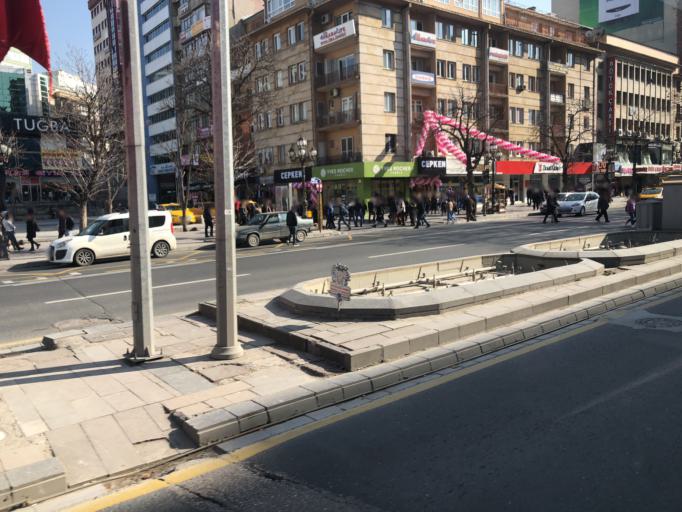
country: TR
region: Ankara
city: Ankara
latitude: 39.9248
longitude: 32.8549
